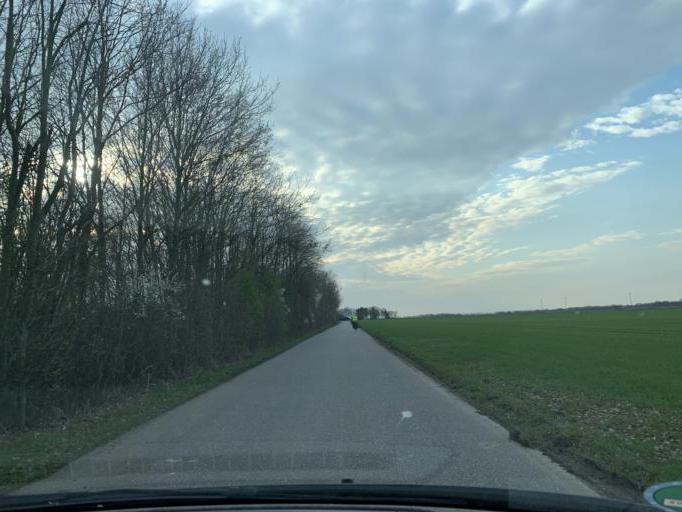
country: DE
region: North Rhine-Westphalia
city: Julich
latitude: 50.9399
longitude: 6.4141
